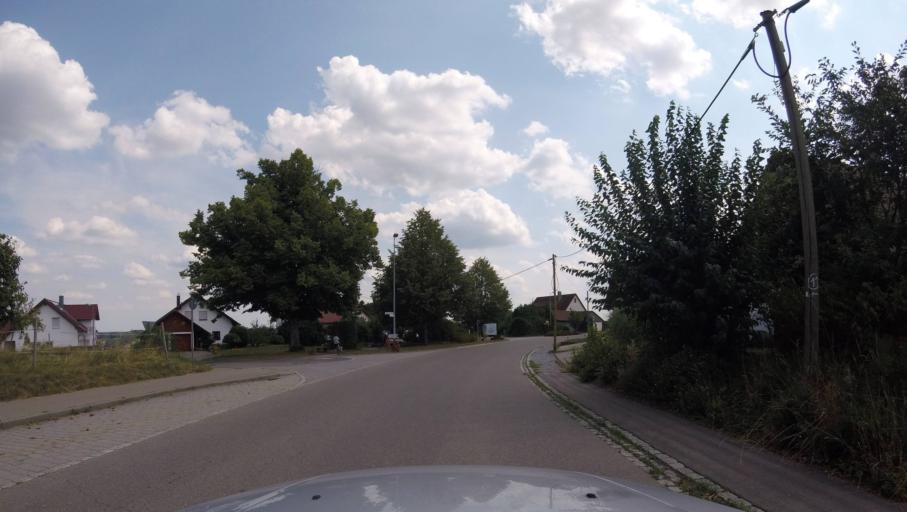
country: DE
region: Baden-Wuerttemberg
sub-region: Regierungsbezirk Stuttgart
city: Spraitbach
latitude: 48.8955
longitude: 9.7239
